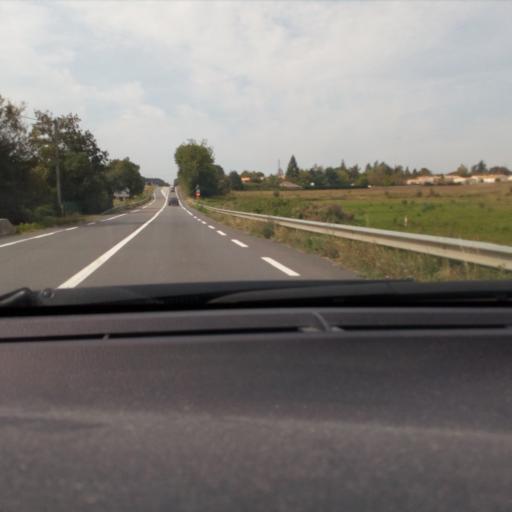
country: FR
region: Poitou-Charentes
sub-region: Departement de la Charente
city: Fleac
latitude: 45.6756
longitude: 0.0898
